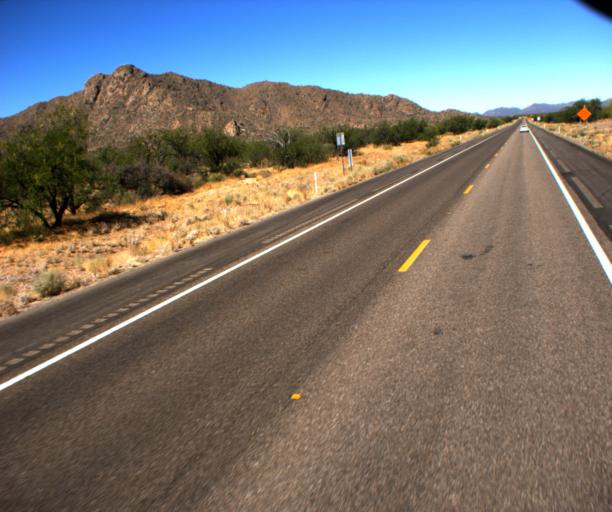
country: US
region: Arizona
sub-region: Pima County
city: Sells
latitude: 32.0127
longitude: -111.6496
